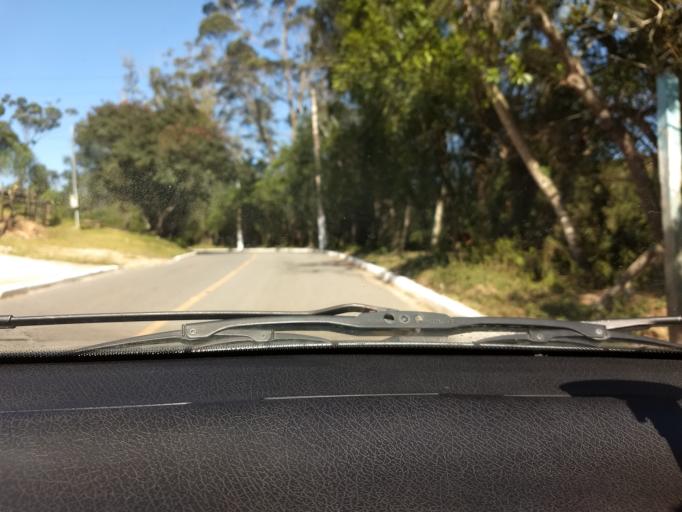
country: BR
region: Sao Paulo
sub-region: Embu-Guacu
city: Embu Guacu
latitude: -23.8099
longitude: -46.7629
